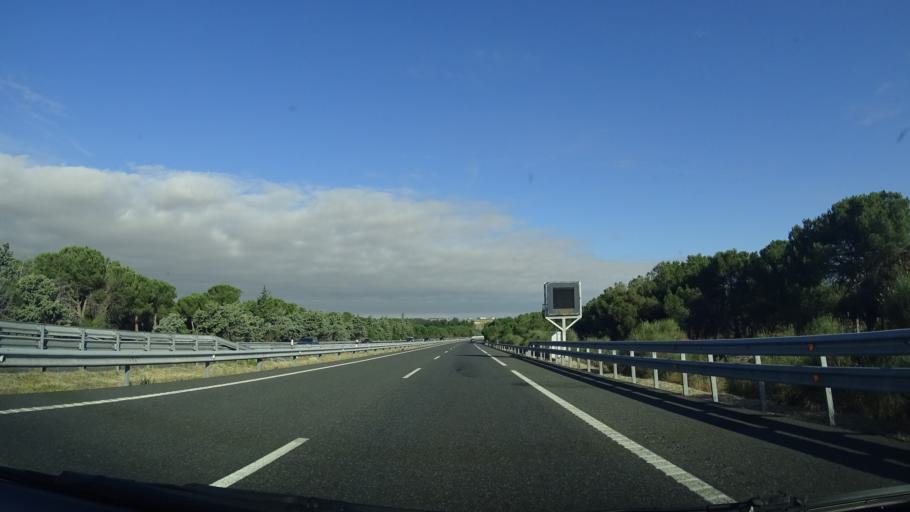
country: ES
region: Castille and Leon
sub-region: Provincia de Avila
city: Sanchidrian
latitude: 40.8607
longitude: -4.5576
